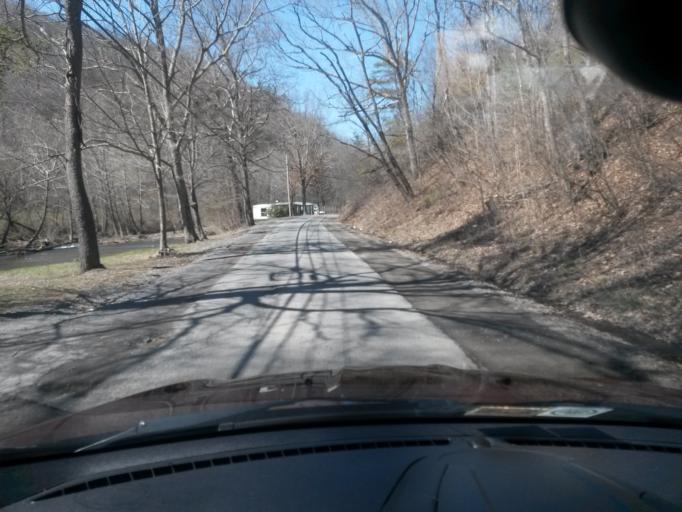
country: US
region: West Virginia
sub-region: Greenbrier County
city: White Sulphur Springs
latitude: 37.7779
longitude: -80.2843
